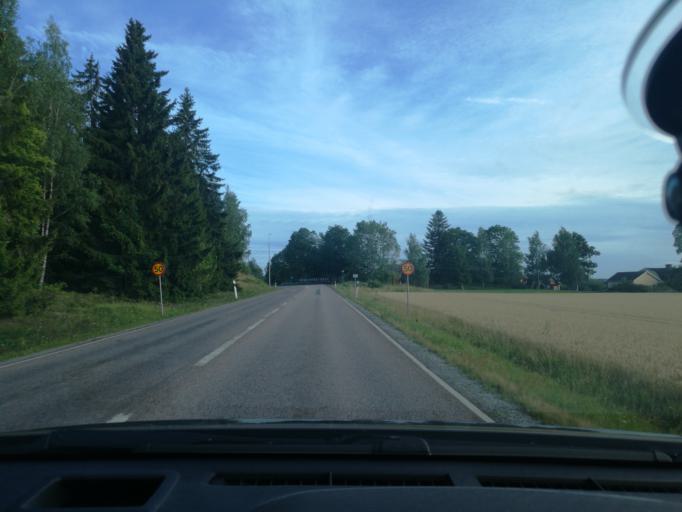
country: SE
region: Vaestmanland
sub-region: Vasteras
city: Vasteras
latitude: 59.6529
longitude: 16.4931
